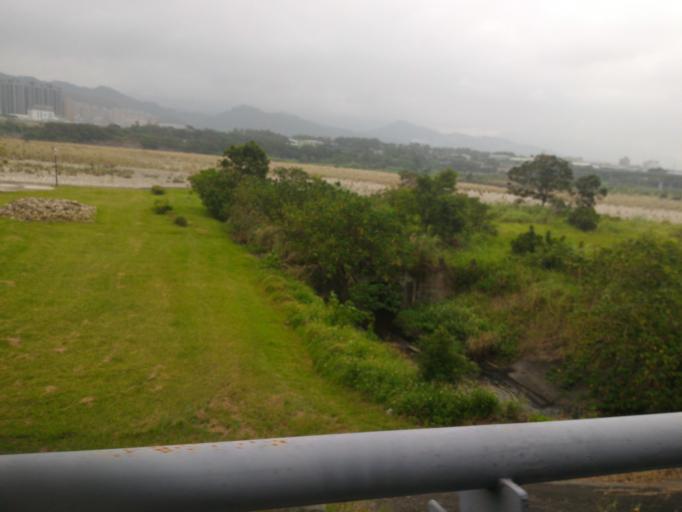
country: TW
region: Taipei
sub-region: Taipei
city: Banqiao
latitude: 24.9695
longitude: 121.4084
